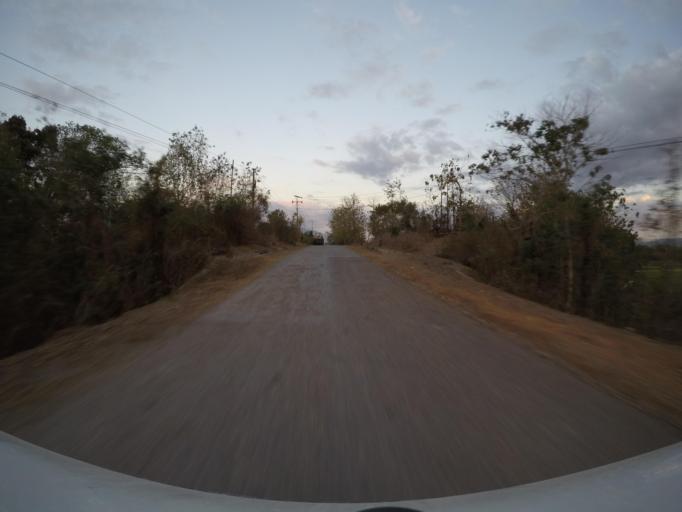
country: TL
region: Bobonaro
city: Maliana
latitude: -8.9615
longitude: 125.1156
